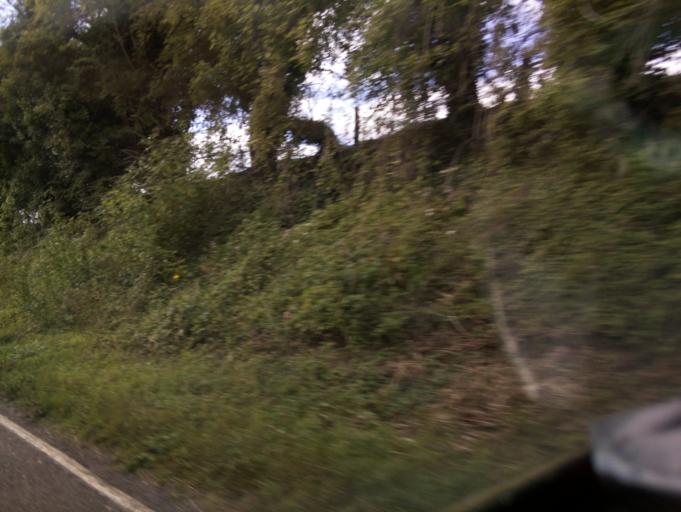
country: GB
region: England
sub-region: Hampshire
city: Abbotts Ann
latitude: 51.1164
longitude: -1.5218
